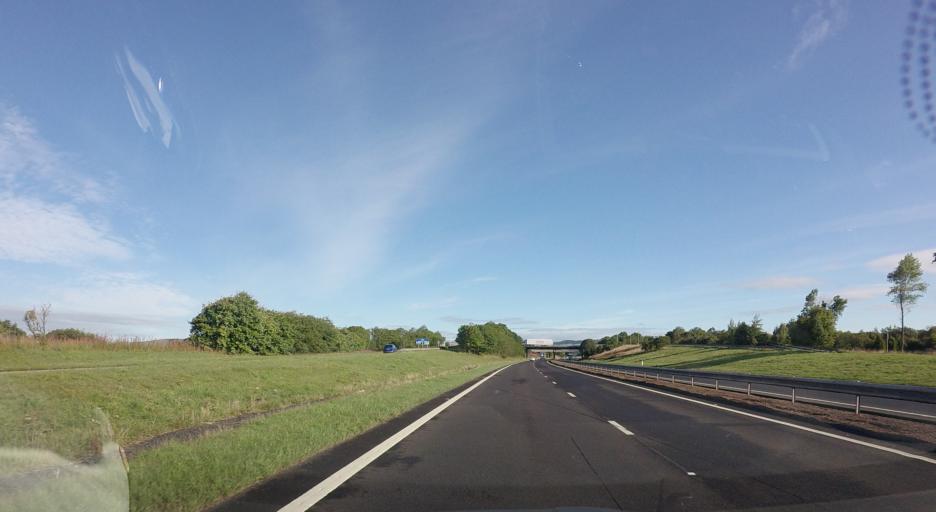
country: GB
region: Scotland
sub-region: Perth and Kinross
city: Kinross
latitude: 56.2051
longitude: -3.4339
